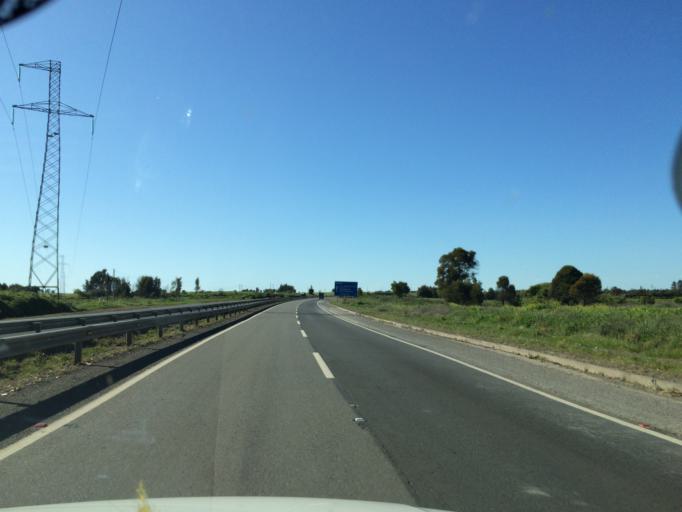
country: CL
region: Biobio
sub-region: Provincia de Biobio
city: Los Angeles
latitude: -37.4613
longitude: -72.4094
